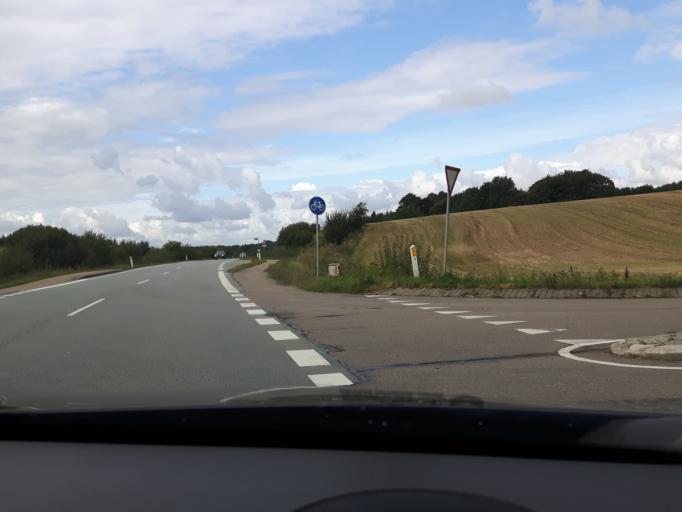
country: DK
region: Central Jutland
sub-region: Hedensted Kommune
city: Hedensted
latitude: 55.7051
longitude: 9.7657
